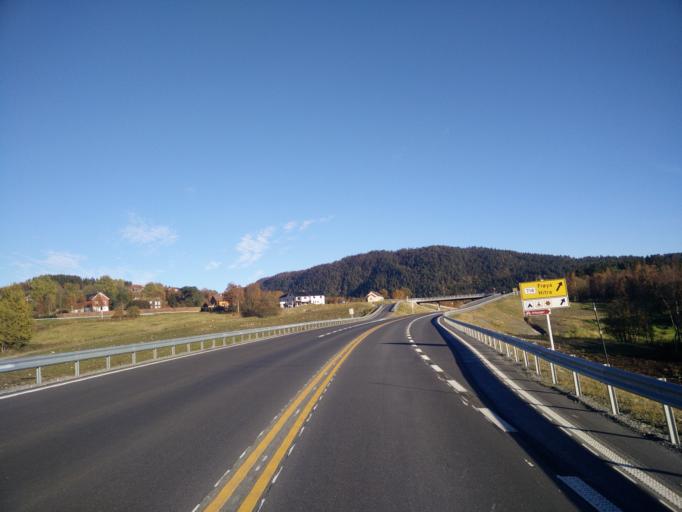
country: NO
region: Sor-Trondelag
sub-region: Snillfjord
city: Krokstadora
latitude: 63.2865
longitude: 9.6245
